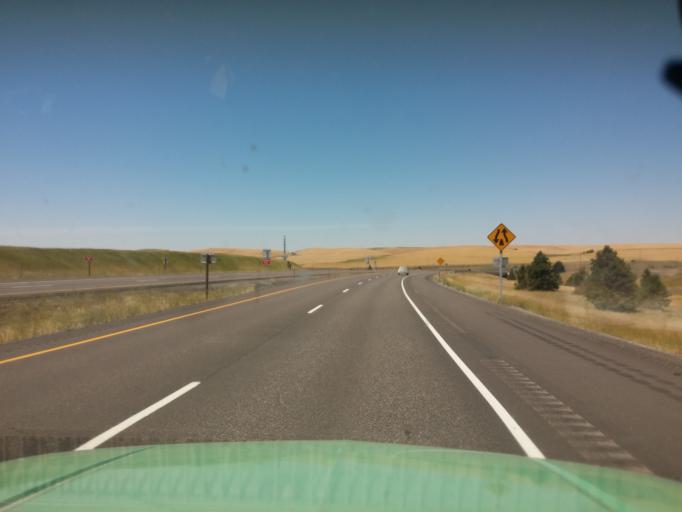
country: US
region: Washington
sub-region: Asotin County
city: Clarkston
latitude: 46.4714
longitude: -117.0339
